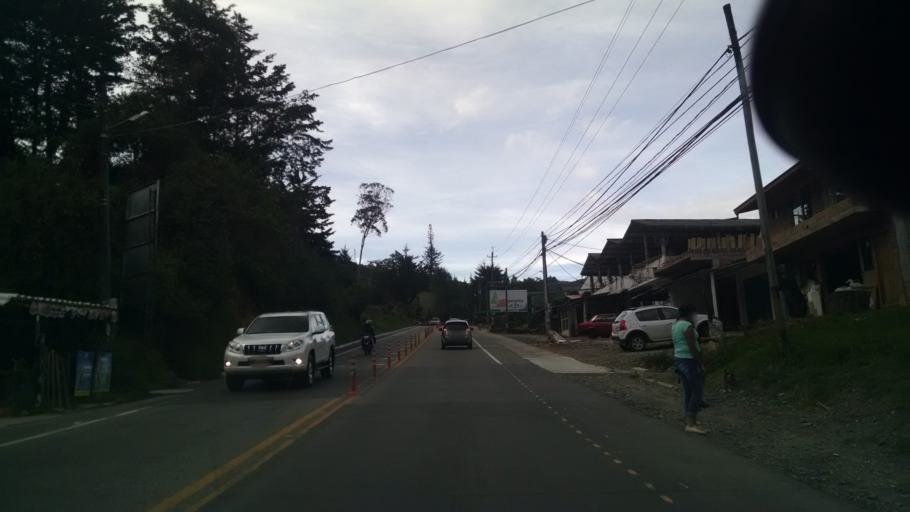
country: CO
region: Antioquia
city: El Retiro
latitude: 6.1161
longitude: -75.5006
